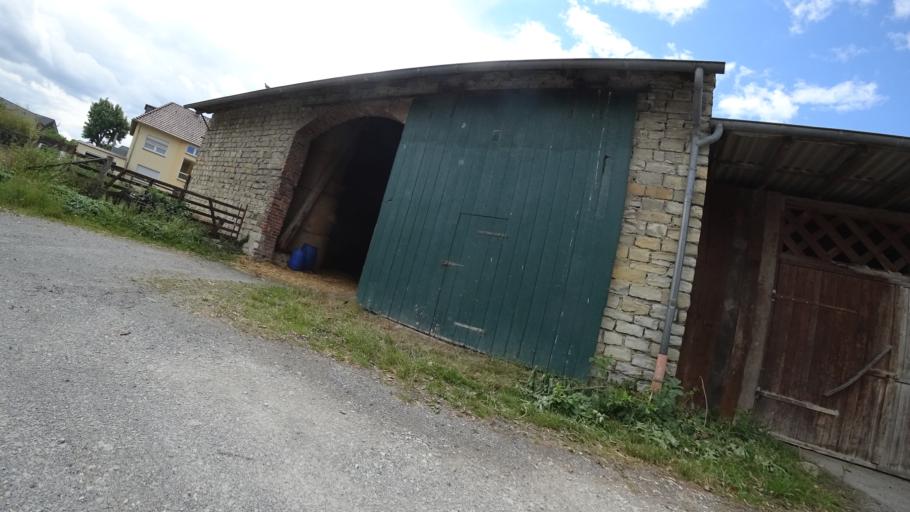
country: DE
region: North Rhine-Westphalia
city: Erwitte
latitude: 51.6271
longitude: 8.3686
